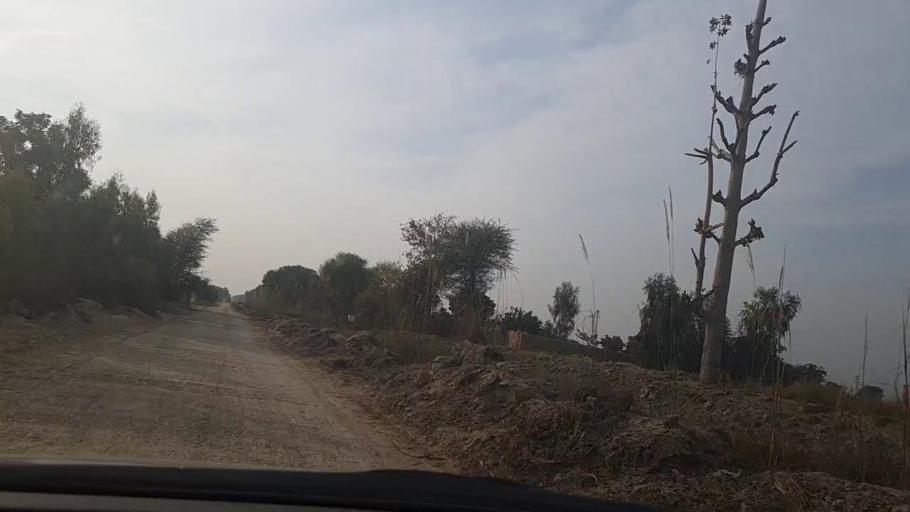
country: PK
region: Sindh
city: Daulatpur
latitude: 26.3340
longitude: 68.0698
